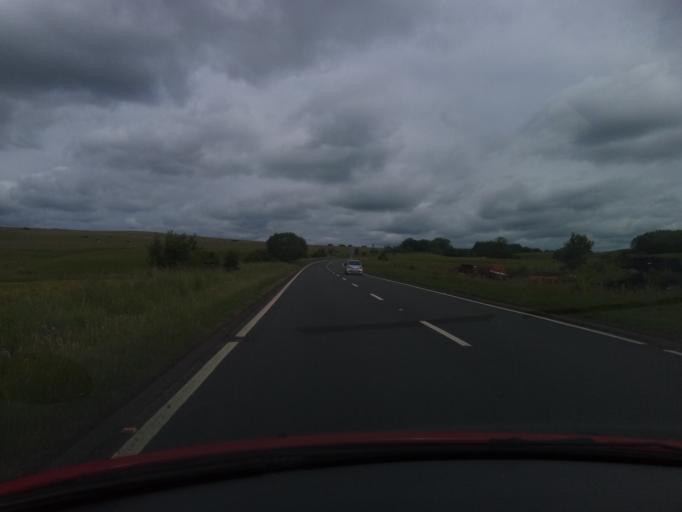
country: GB
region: Scotland
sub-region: The Scottish Borders
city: Hawick
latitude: 55.4521
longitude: -2.7788
